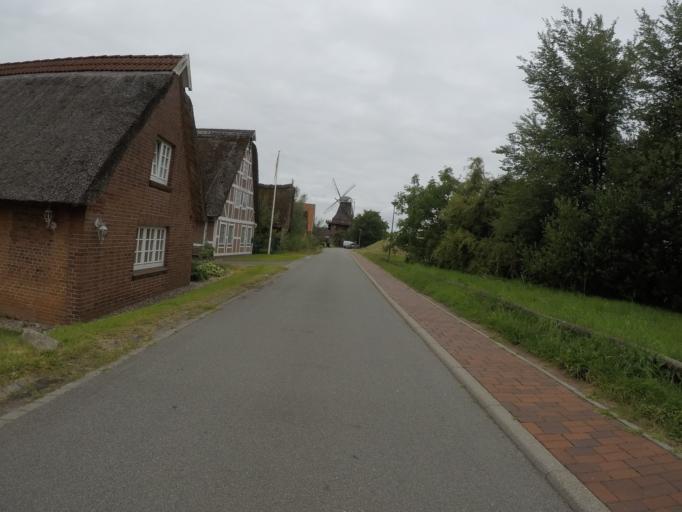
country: DE
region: Lower Saxony
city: Jork
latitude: 53.5393
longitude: 9.6955
